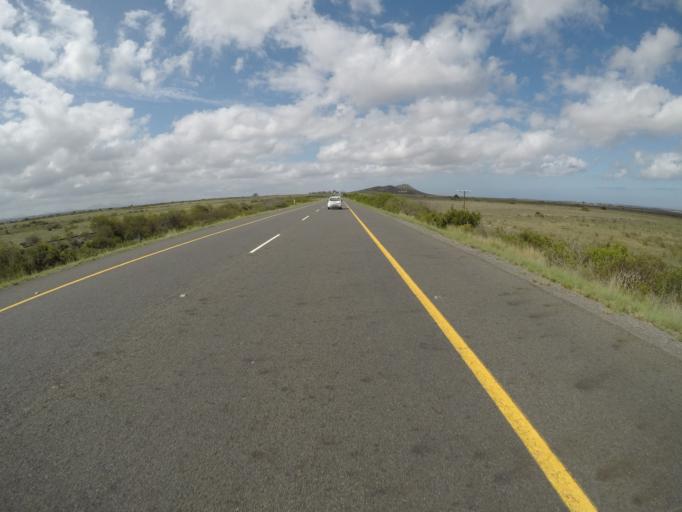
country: ZA
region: Western Cape
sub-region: Eden District Municipality
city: Mossel Bay
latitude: -34.1847
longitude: 21.8617
